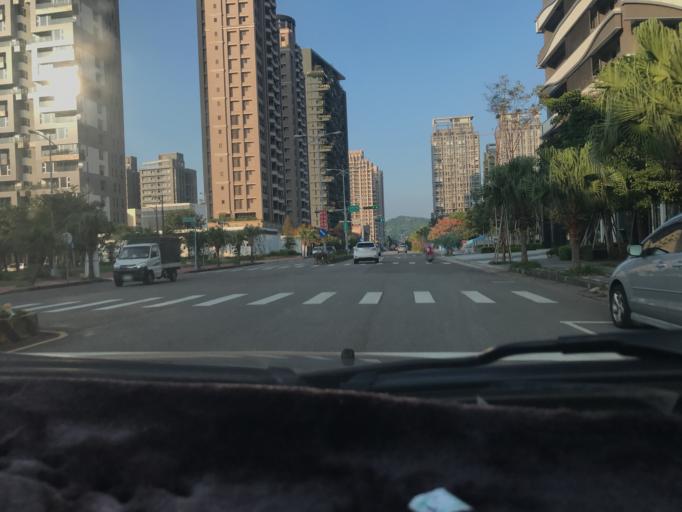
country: TW
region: Taiwan
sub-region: Hsinchu
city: Zhubei
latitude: 24.8091
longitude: 121.0332
